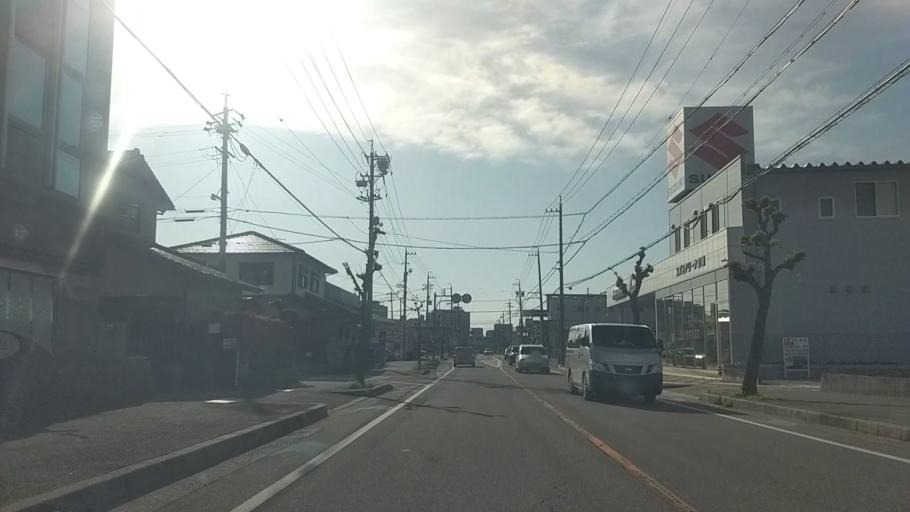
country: JP
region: Aichi
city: Anjo
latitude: 34.9655
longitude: 137.0686
